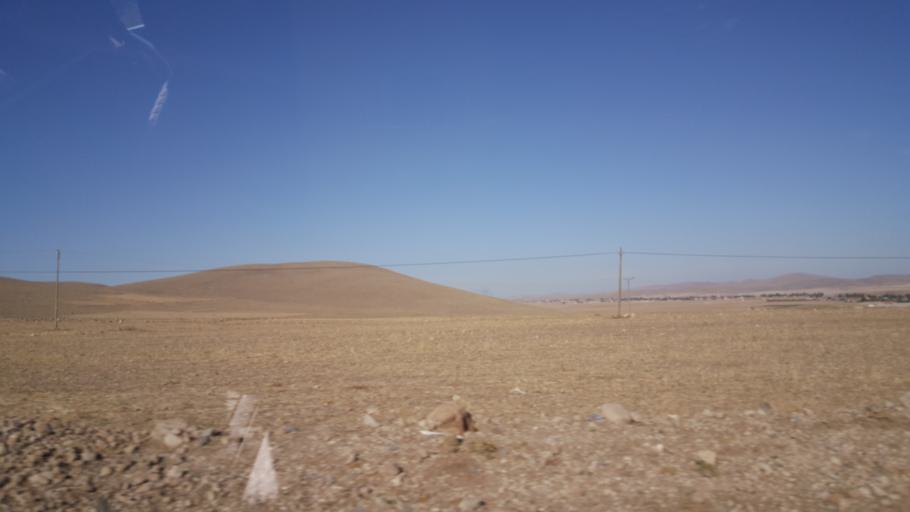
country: TR
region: Ankara
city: Altpinar
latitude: 39.1693
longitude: 32.7169
